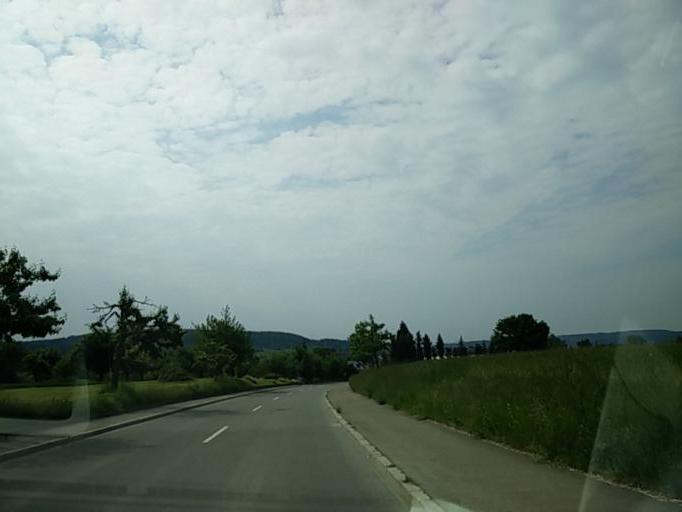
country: DE
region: Baden-Wuerttemberg
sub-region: Tuebingen Region
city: Hirrlingen
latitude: 48.4164
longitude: 8.8866
